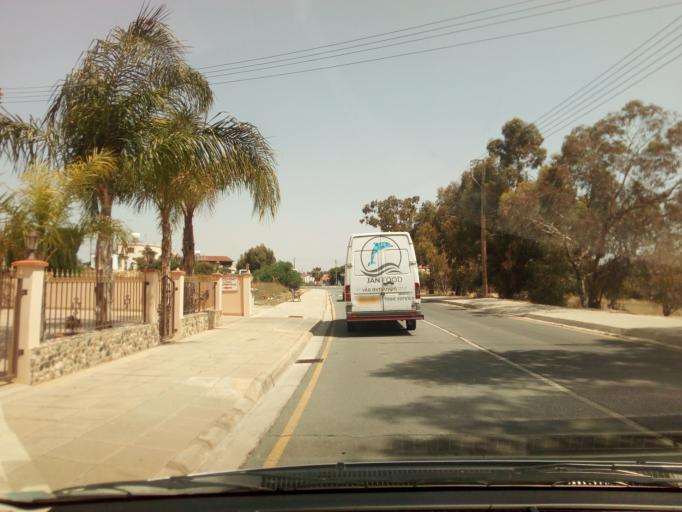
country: CY
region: Larnaka
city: Xylotymbou
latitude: 34.9866
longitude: 33.7805
